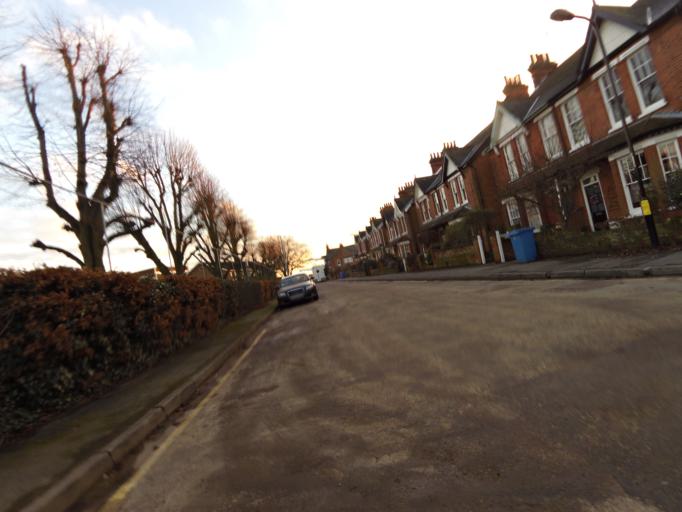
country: GB
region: England
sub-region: Suffolk
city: Ipswich
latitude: 52.0651
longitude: 1.1492
